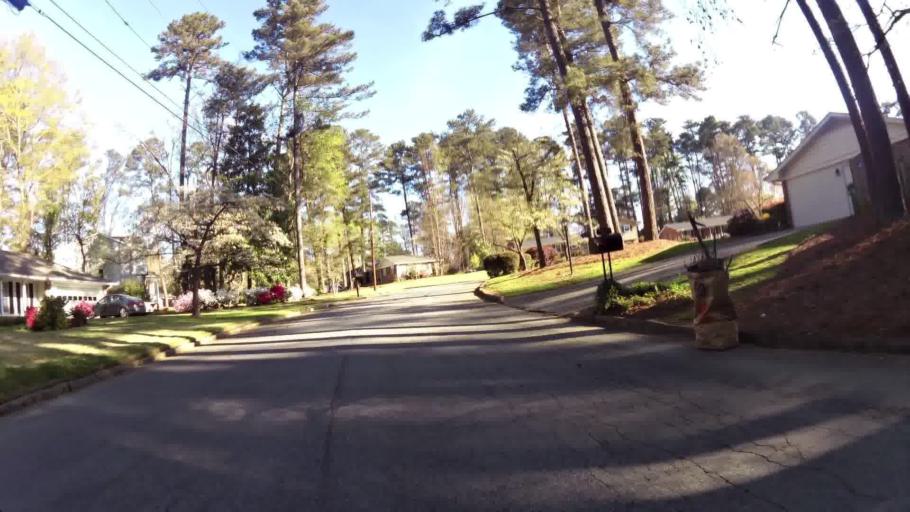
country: US
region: Georgia
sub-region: DeKalb County
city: Clarkston
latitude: 33.8367
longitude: -84.2648
